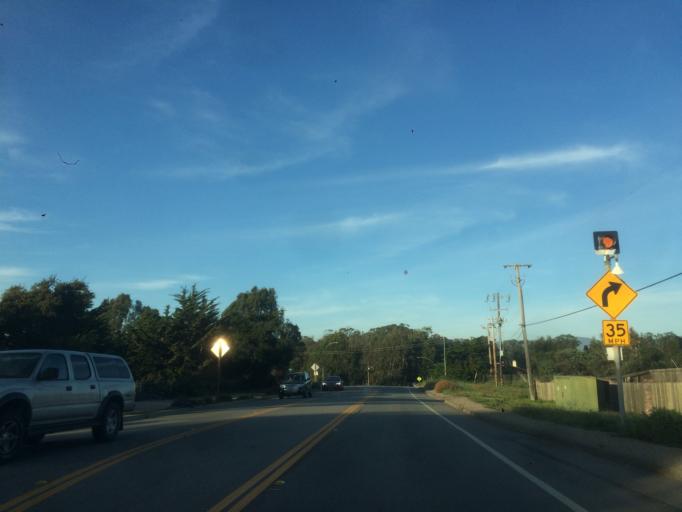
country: US
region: California
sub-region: San Luis Obispo County
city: Los Osos
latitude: 35.3110
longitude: -120.8541
